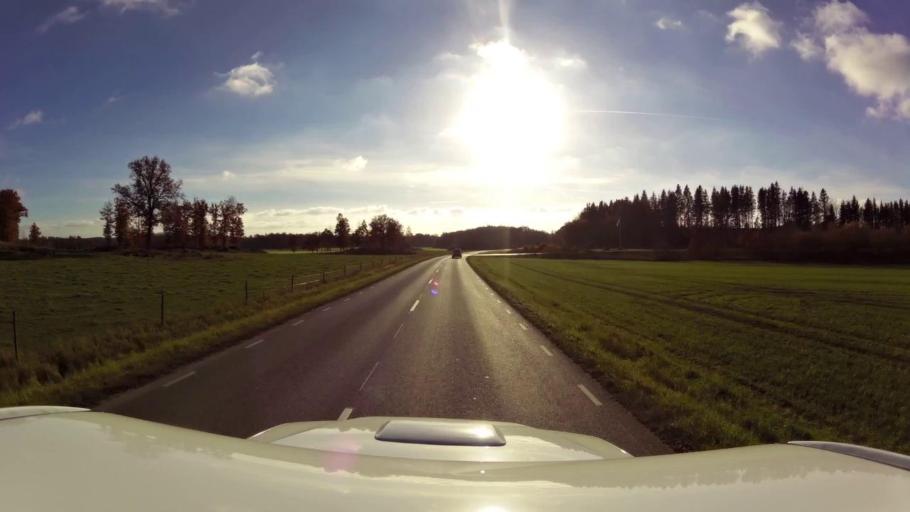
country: SE
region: OEstergoetland
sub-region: Linkopings Kommun
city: Malmslatt
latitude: 58.3310
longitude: 15.5114
